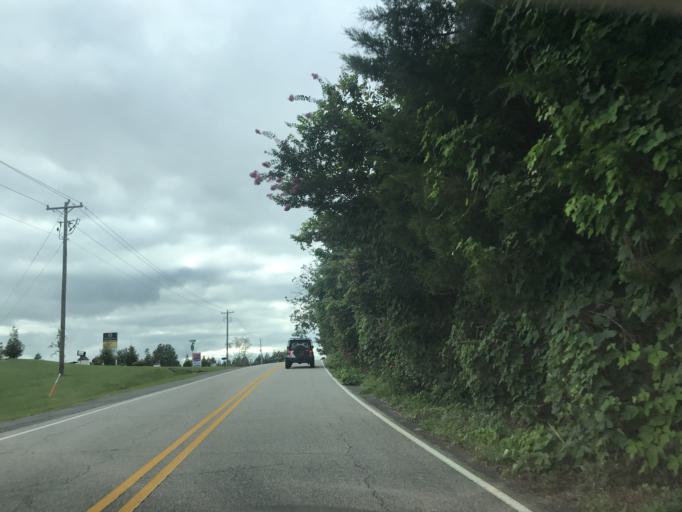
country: US
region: North Carolina
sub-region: Johnston County
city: Clayton
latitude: 35.5717
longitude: -78.5568
